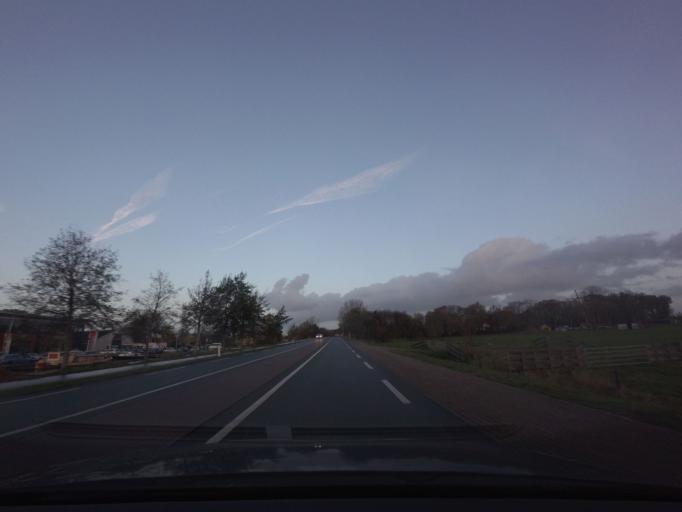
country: NL
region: South Holland
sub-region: Gemeente Teylingen
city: Sassenheim
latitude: 52.2254
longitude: 4.5342
